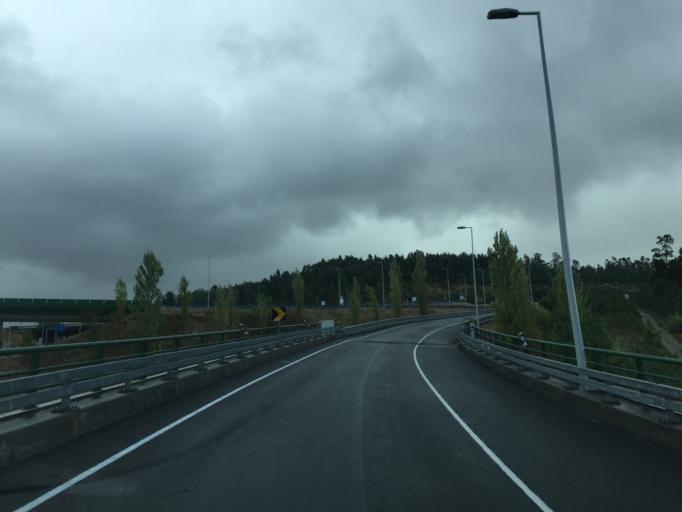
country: PT
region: Aveiro
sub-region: Mealhada
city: Pampilhosa do Botao
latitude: 40.2735
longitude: -8.4851
